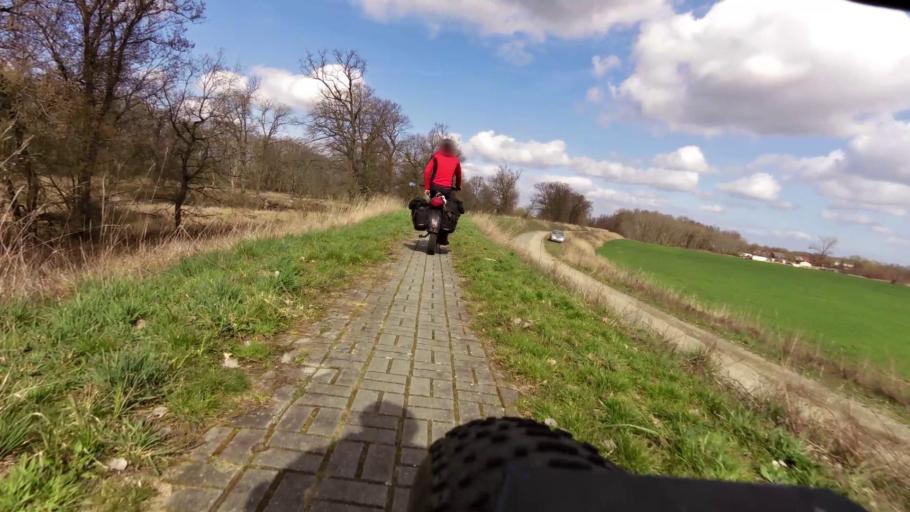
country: DE
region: Brandenburg
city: Lebus
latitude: 52.3998
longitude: 14.5425
